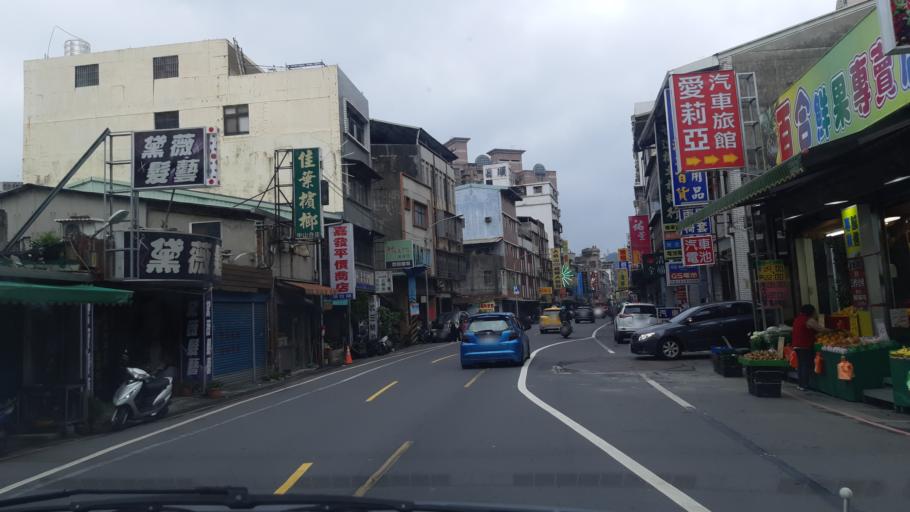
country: TW
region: Taiwan
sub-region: Taoyuan
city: Taoyuan
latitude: 24.9367
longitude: 121.3642
